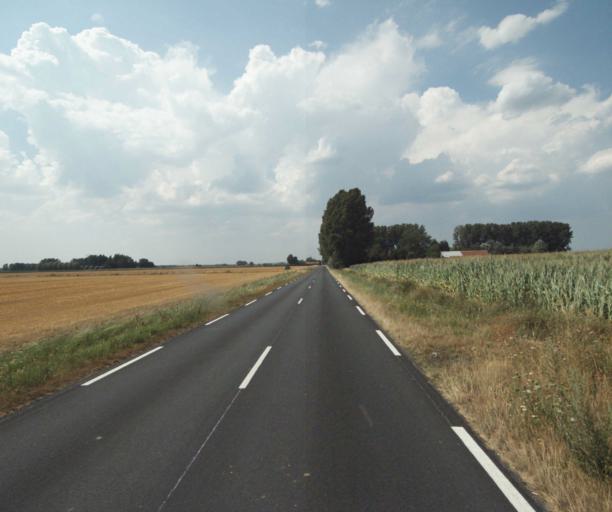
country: FR
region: Nord-Pas-de-Calais
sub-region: Departement du Nord
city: Quesnoy-sur-Deule
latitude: 50.7235
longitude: 2.9819
